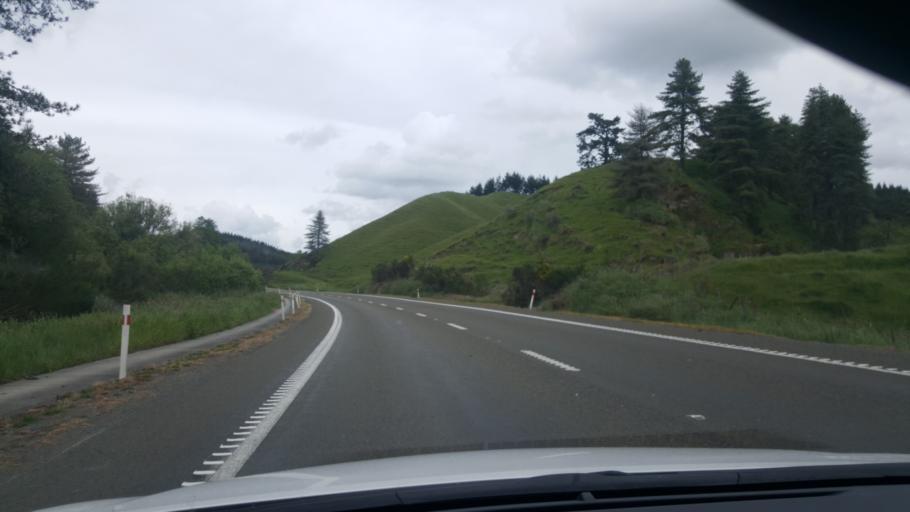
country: NZ
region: Bay of Plenty
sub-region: Rotorua District
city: Rotorua
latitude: -38.2213
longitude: 176.2834
